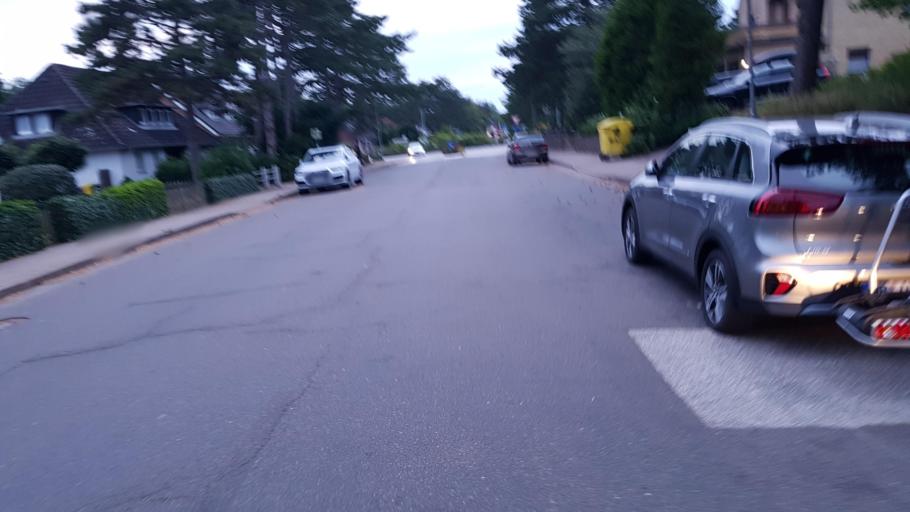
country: DE
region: Schleswig-Holstein
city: Sankt Peter-Ording
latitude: 54.3089
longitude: 8.6162
